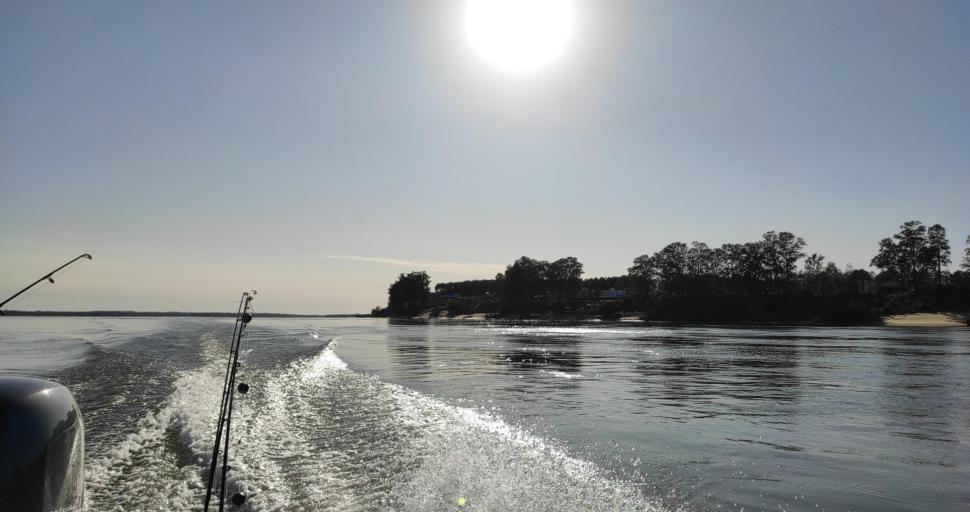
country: AR
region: Corrientes
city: Ituzaingo
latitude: -27.6006
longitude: -56.8192
